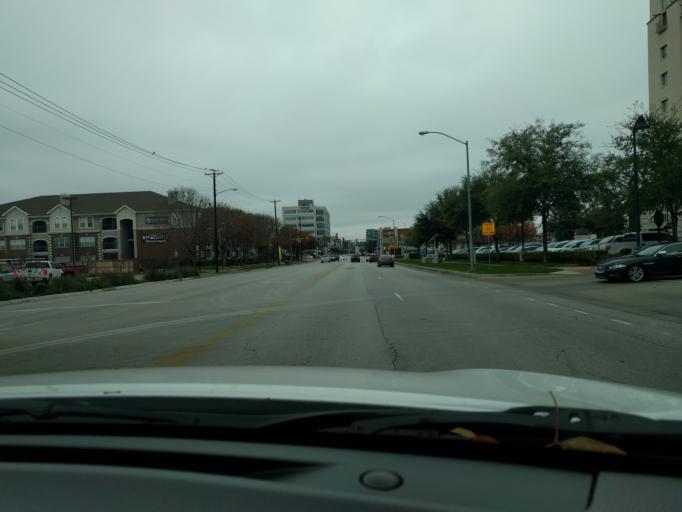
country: US
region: Texas
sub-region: Tarrant County
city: Fort Worth
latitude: 32.7511
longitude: -97.3531
